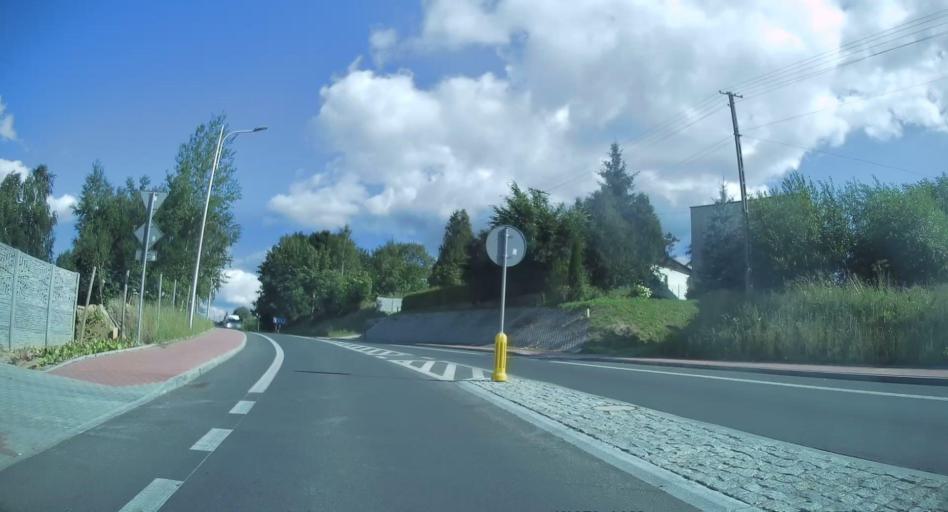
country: PL
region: Swietokrzyskie
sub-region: Powiat kielecki
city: Bodzentyn
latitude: 50.9390
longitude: 20.9501
